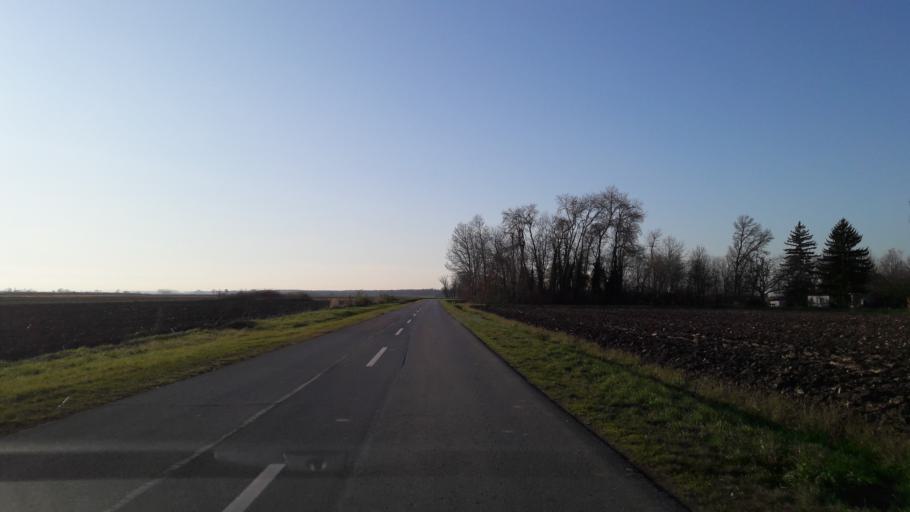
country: HR
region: Osjecko-Baranjska
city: Vuka
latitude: 45.4220
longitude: 18.5206
